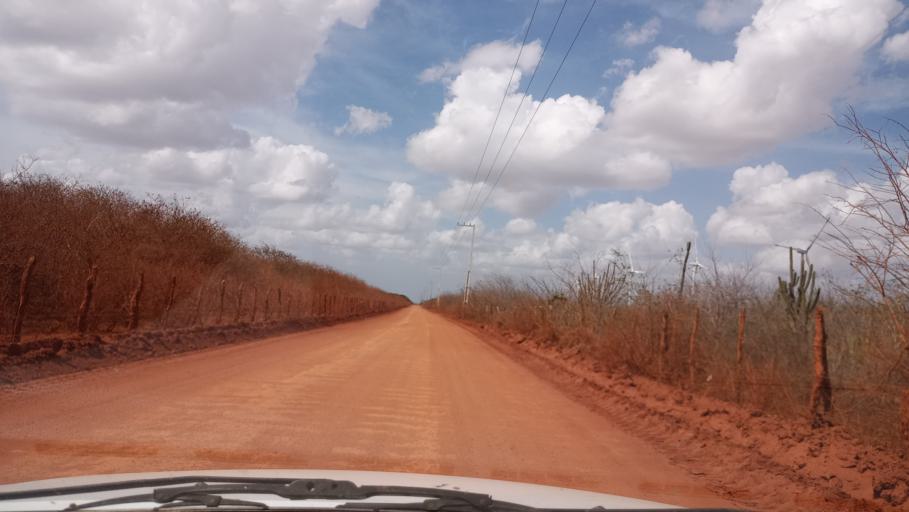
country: BR
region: Rio Grande do Norte
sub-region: Joao Camara
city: Joao Camara
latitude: -5.3614
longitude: -35.8351
